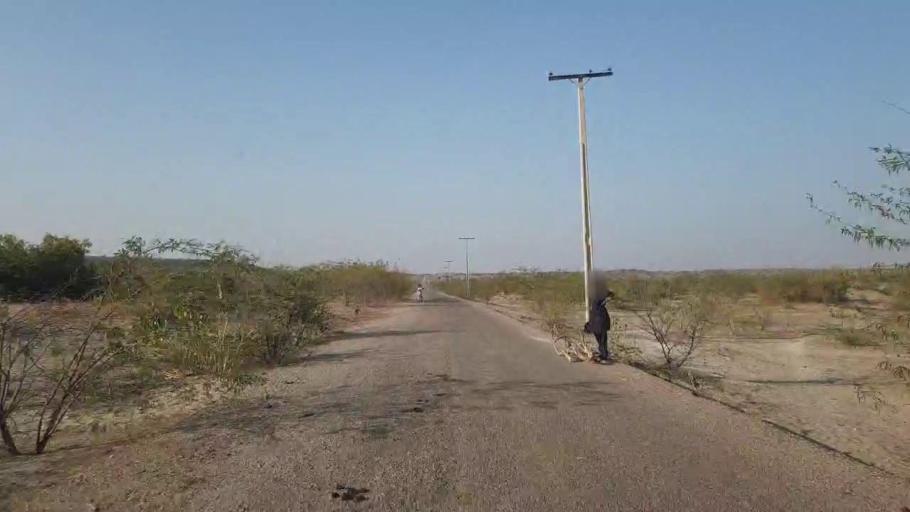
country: PK
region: Sindh
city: Chor
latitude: 25.5967
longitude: 69.8380
